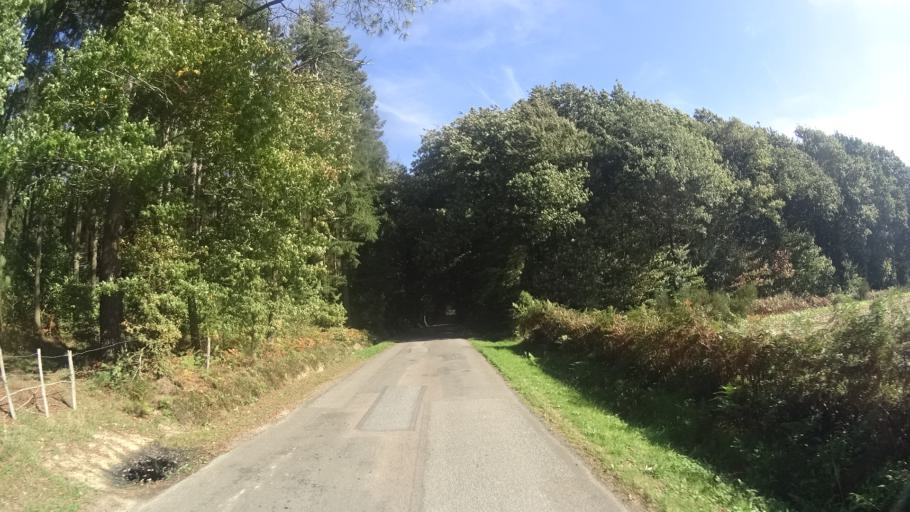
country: FR
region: Brittany
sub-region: Departement du Morbihan
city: La Gacilly
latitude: 47.7470
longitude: -2.1643
